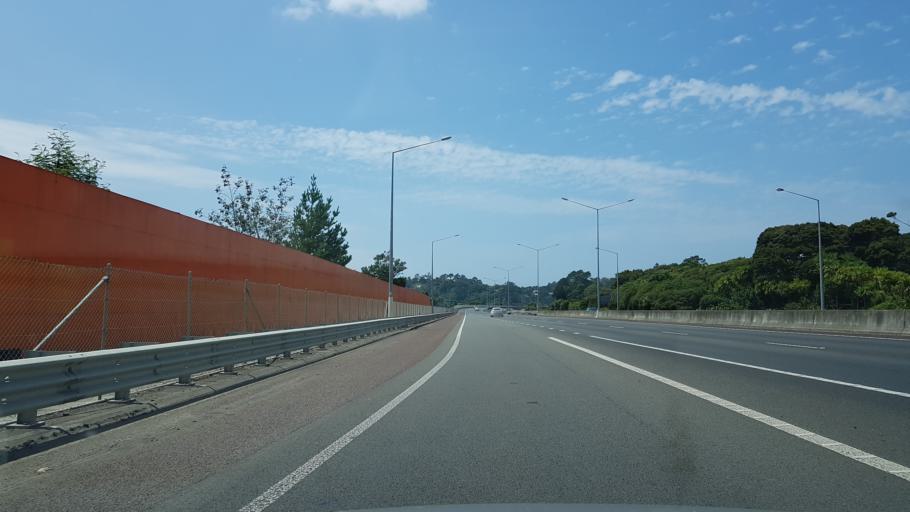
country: NZ
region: Auckland
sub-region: Auckland
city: Rosebank
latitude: -36.7892
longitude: 174.6574
